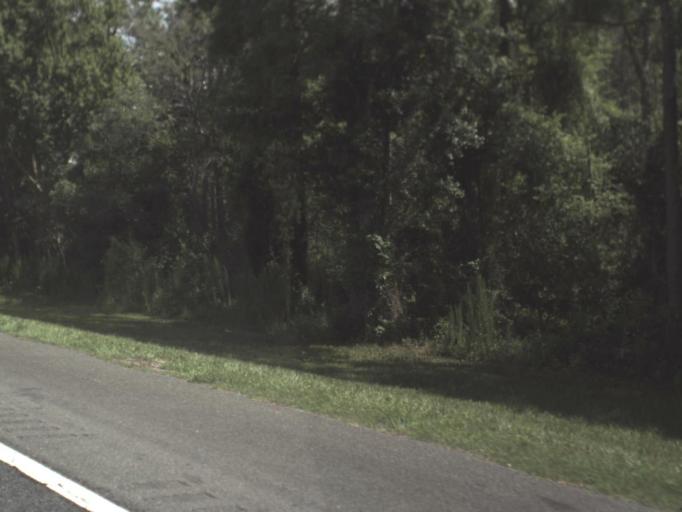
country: US
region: Florida
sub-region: Columbia County
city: Lake City
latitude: 30.1287
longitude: -82.6620
